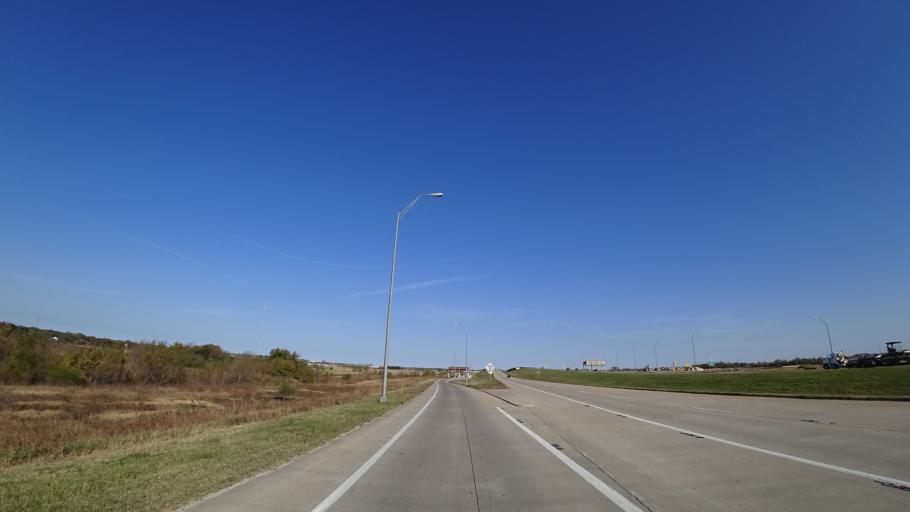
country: US
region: Texas
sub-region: Williamson County
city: Hutto
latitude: 30.5281
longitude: -97.5764
